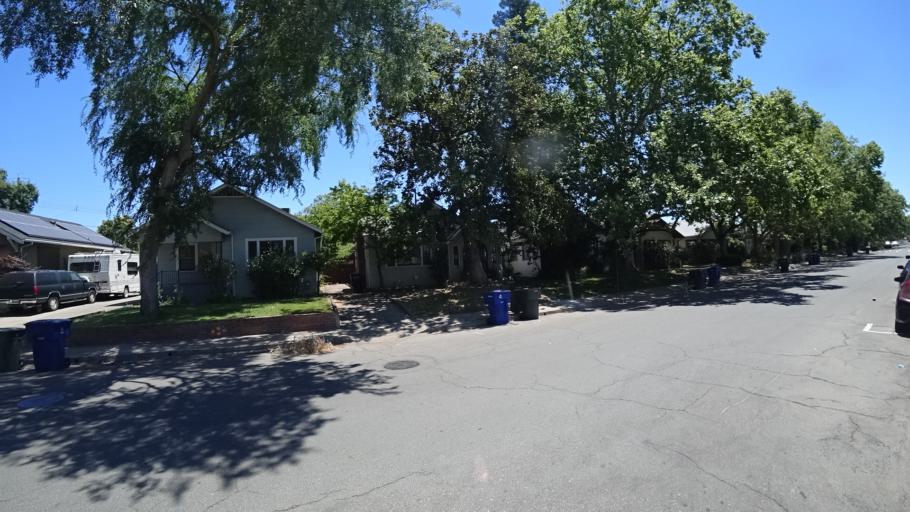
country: US
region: California
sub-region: Sacramento County
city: Sacramento
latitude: 38.5576
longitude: -121.4641
